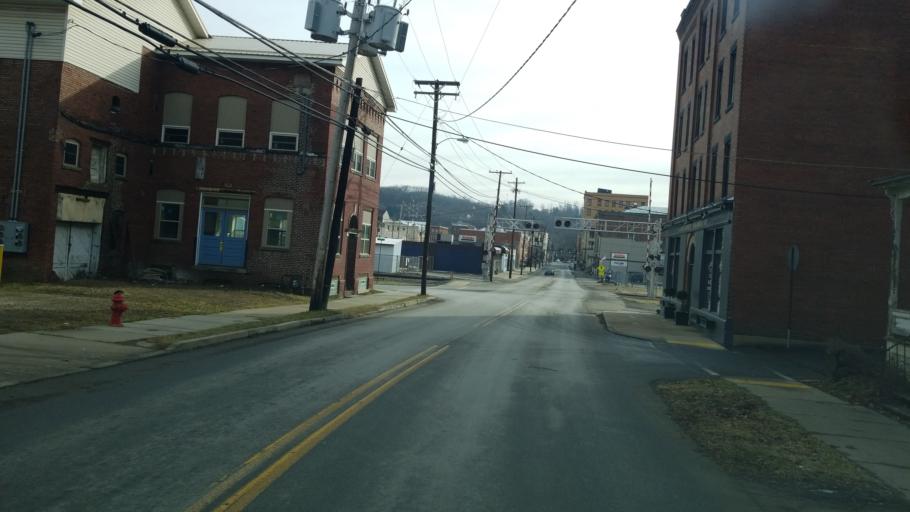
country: US
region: Pennsylvania
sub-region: Jefferson County
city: Punxsutawney
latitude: 40.9466
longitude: -78.9726
